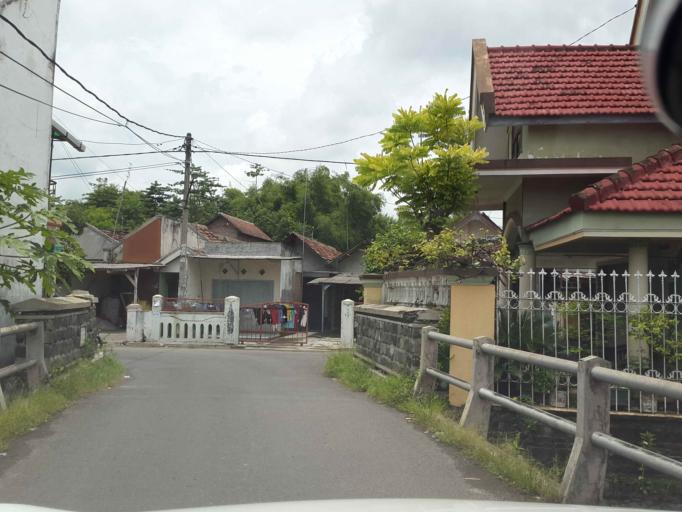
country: ID
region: East Java
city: Soko
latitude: -7.4678
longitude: 112.4130
